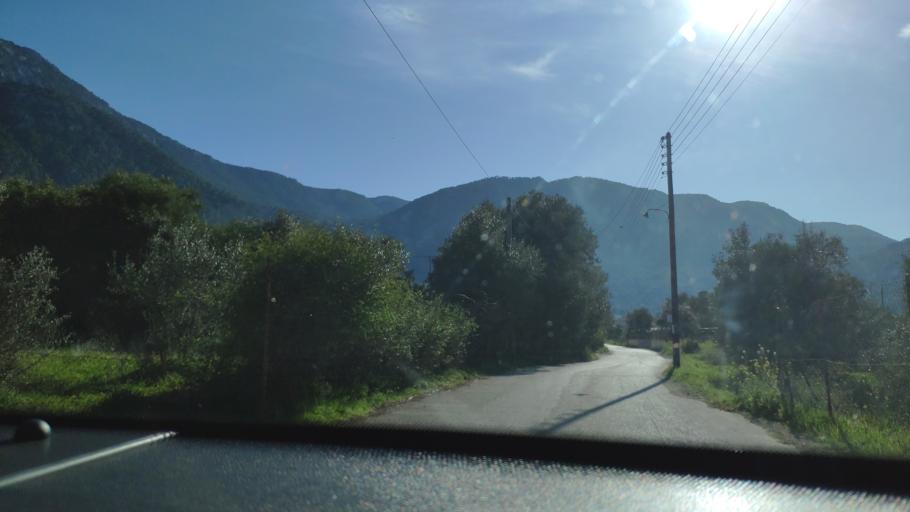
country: GR
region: Peloponnese
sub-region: Nomos Korinthias
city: Perachora
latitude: 38.0502
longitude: 23.0347
